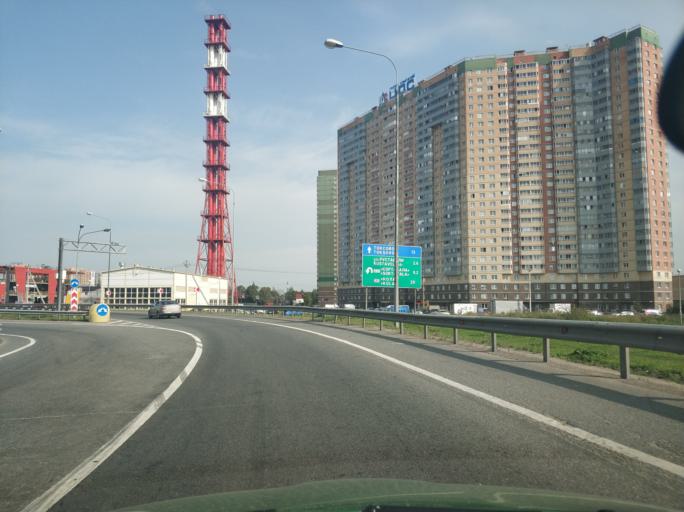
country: RU
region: Leningrad
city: Murino
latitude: 60.0395
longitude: 30.4447
